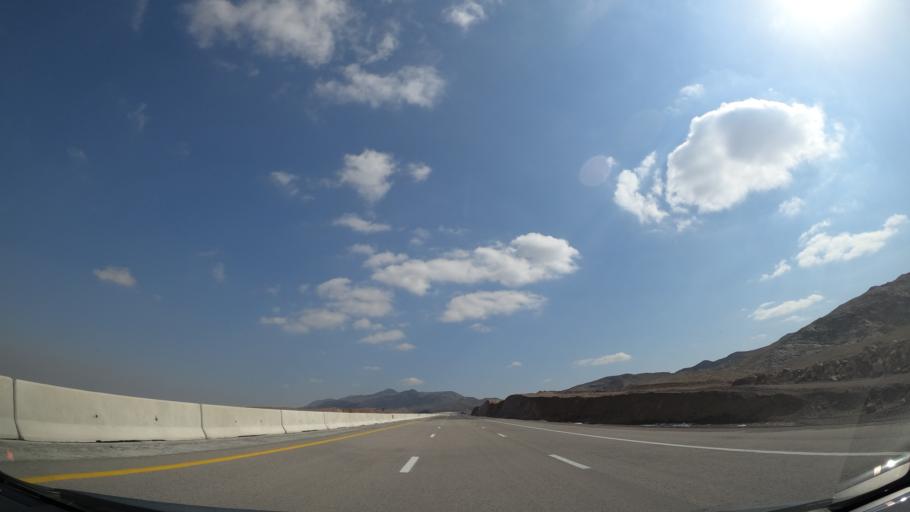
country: IR
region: Alborz
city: Nazarabad
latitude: 35.7001
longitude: 50.6217
